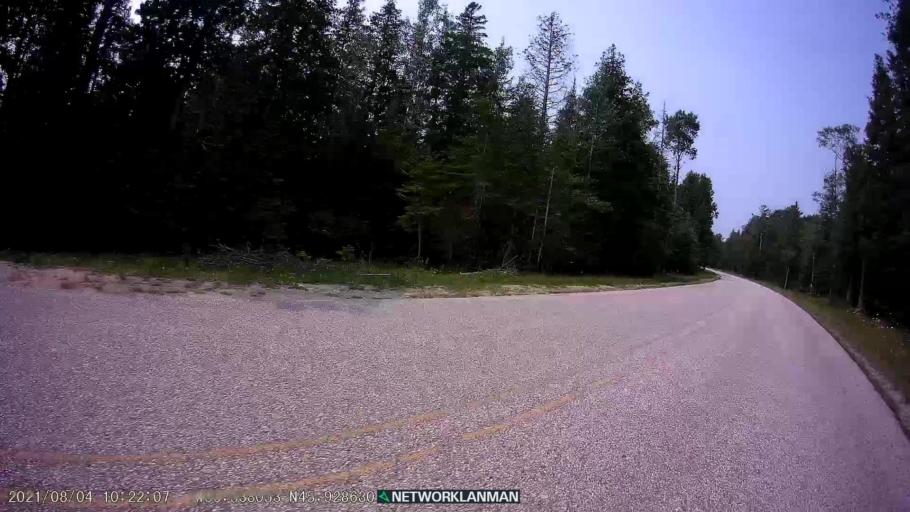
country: CA
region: Ontario
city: Thessalon
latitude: 45.9288
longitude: -83.5383
